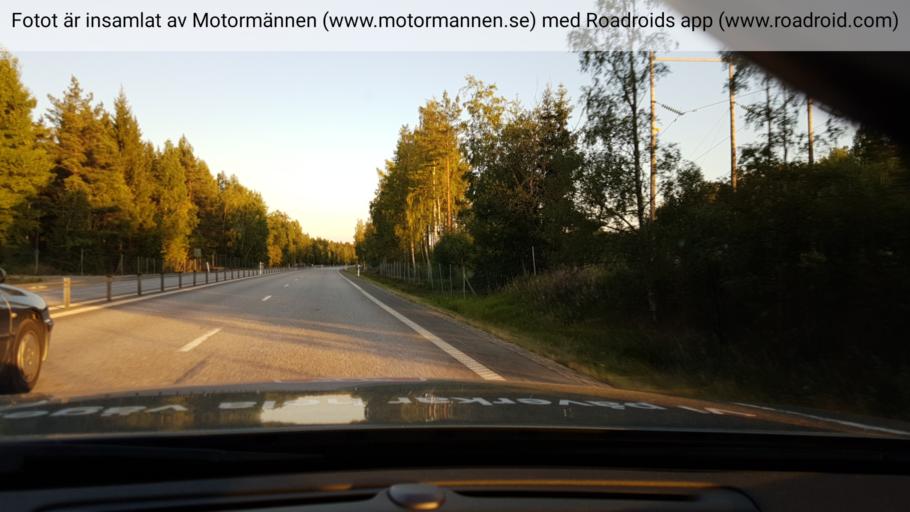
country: SE
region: Vaestmanland
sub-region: Surahammars Kommun
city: Surahammar
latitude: 59.7149
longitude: 16.2422
